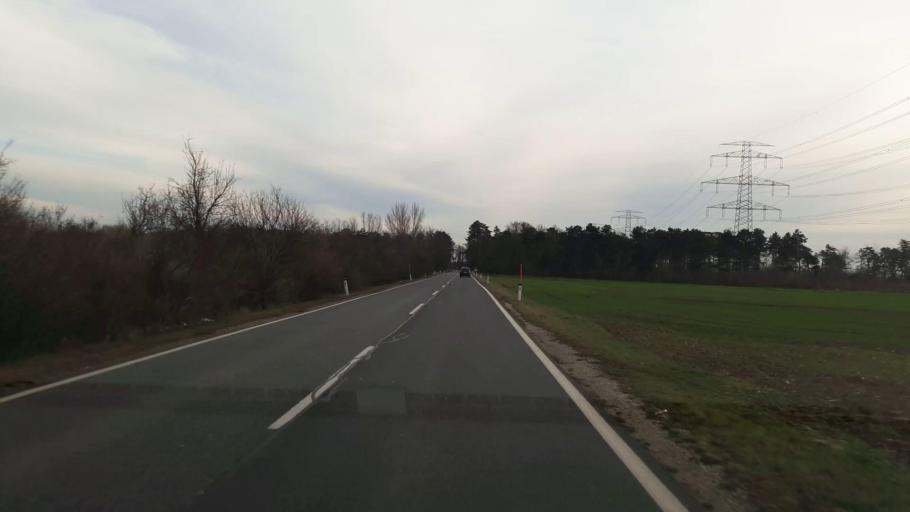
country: AT
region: Lower Austria
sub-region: Politischer Bezirk Ganserndorf
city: Aderklaa
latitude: 48.3083
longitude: 16.5383
